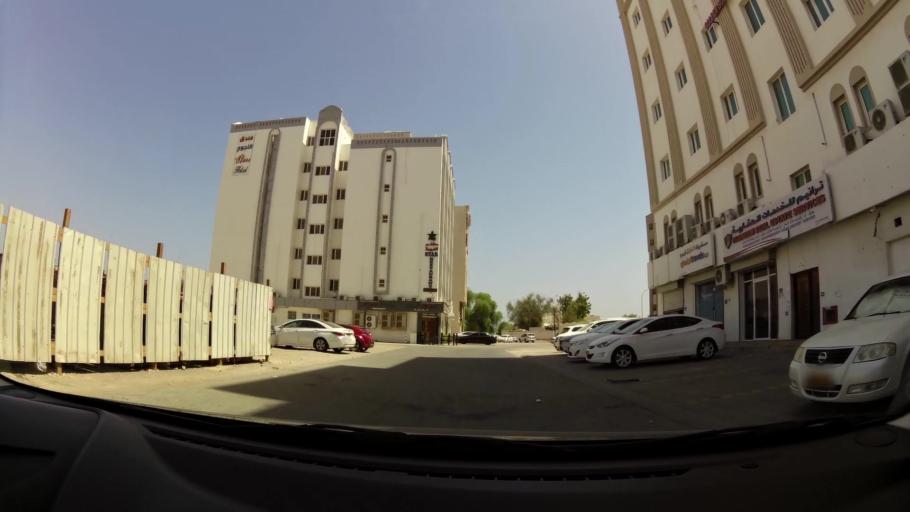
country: OM
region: Muhafazat Masqat
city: Bawshar
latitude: 23.5922
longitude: 58.3997
